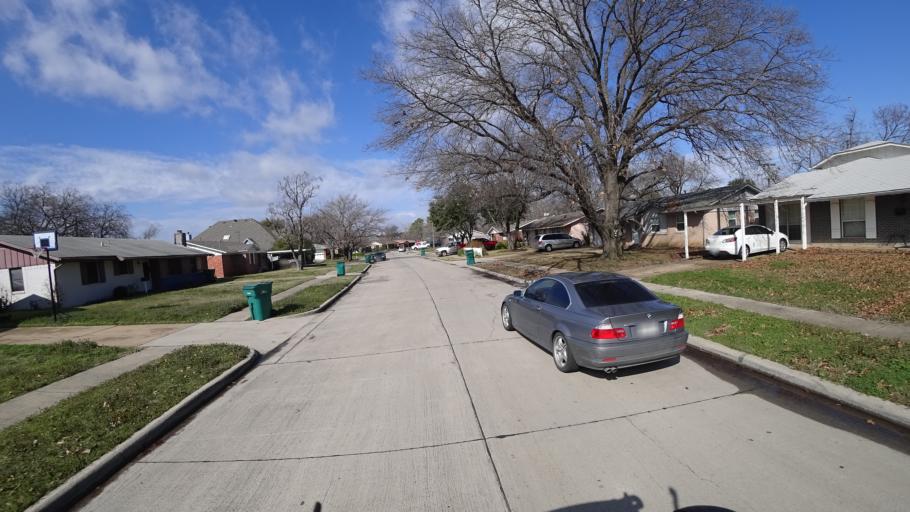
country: US
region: Texas
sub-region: Denton County
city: Lewisville
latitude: 33.0308
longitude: -97.0004
